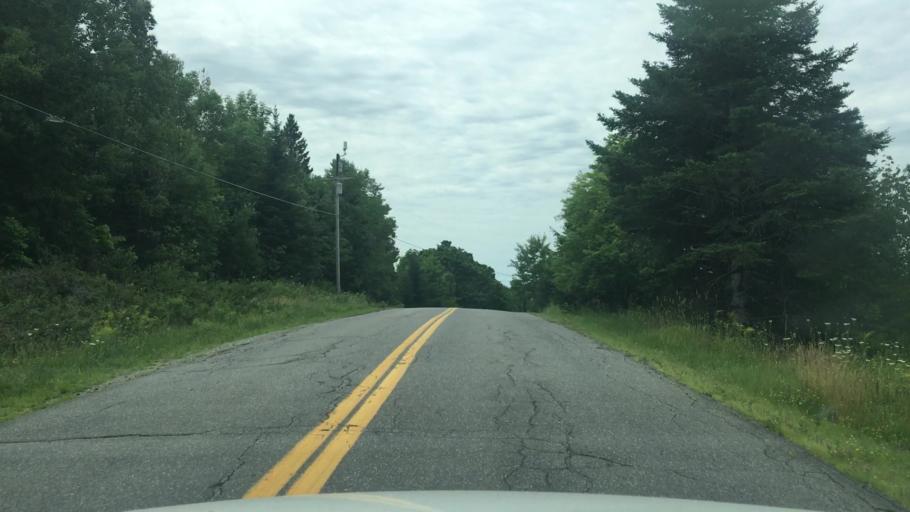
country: US
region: Maine
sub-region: Kennebec County
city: Albion
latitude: 44.4963
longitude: -69.3701
